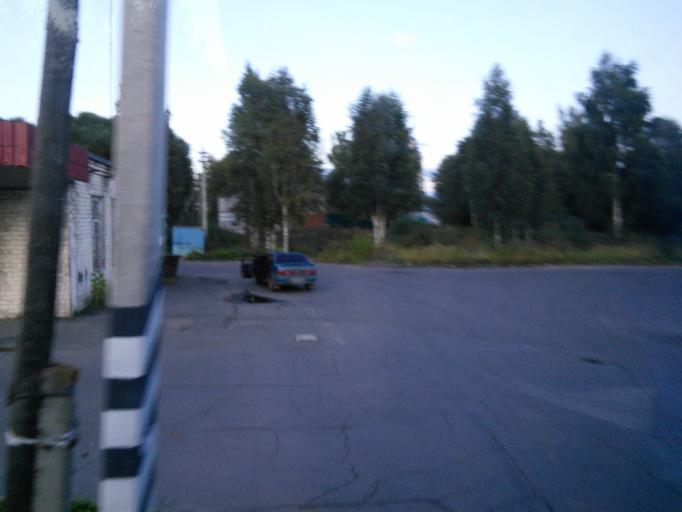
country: RU
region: Jaroslavl
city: Poshekhon'ye
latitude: 58.4973
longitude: 39.1242
